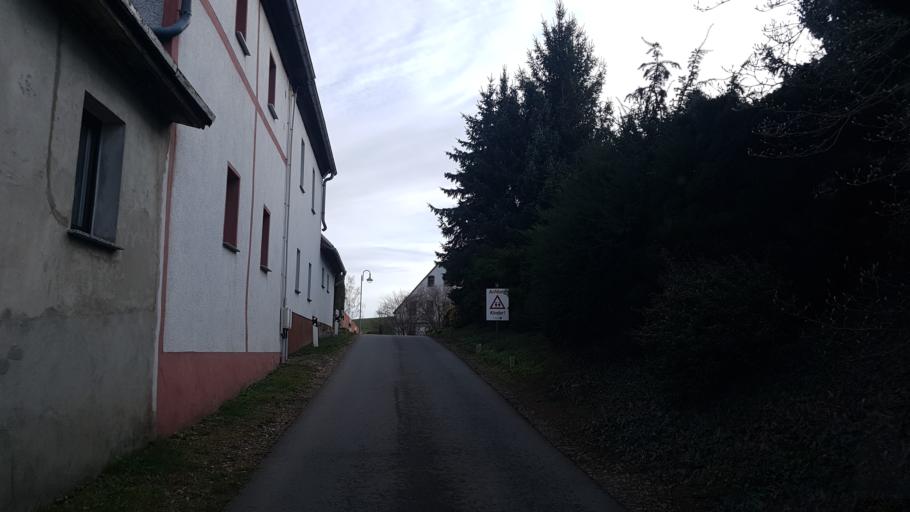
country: DE
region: Saxony
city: Ostrau
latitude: 51.1836
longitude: 13.1734
